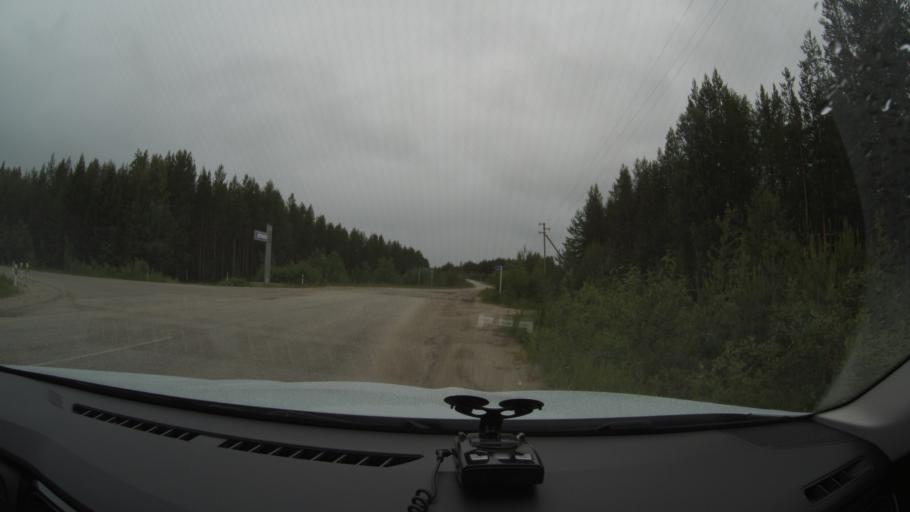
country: RU
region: Komi Republic
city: Kozhva
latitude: 65.1095
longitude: 57.0084
